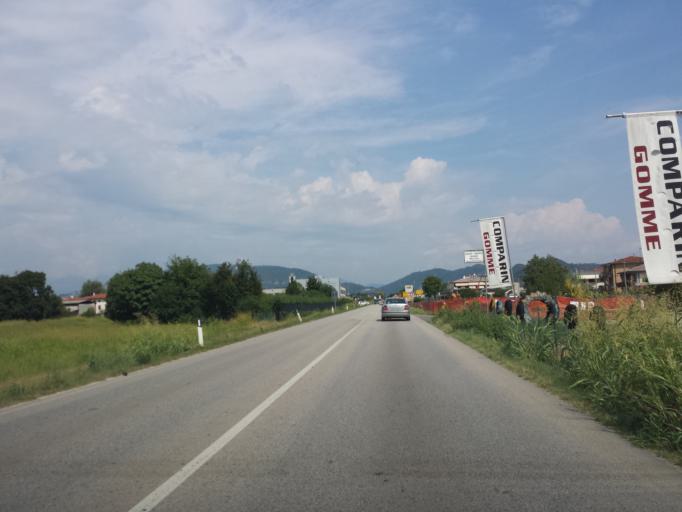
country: IT
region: Veneto
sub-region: Provincia di Vicenza
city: Trissino
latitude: 45.5625
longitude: 11.3848
